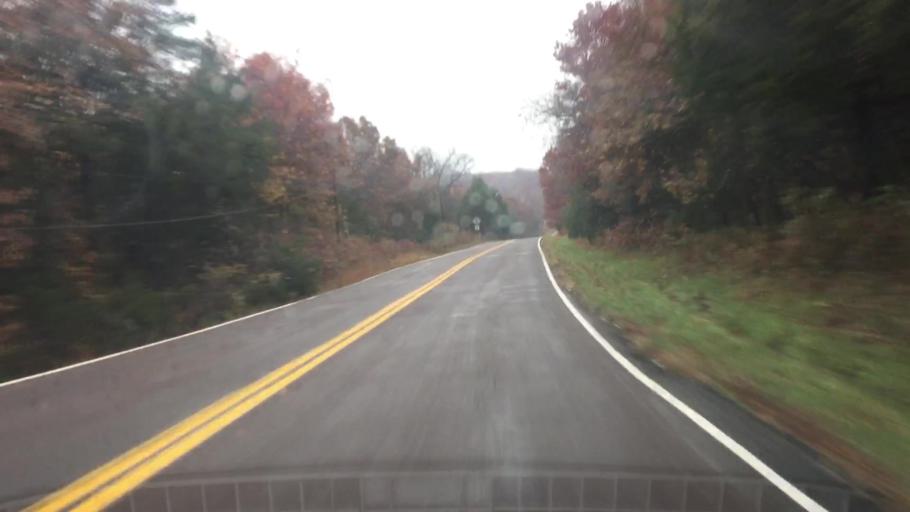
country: US
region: Missouri
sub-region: Boone County
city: Columbia
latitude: 38.8719
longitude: -92.3232
